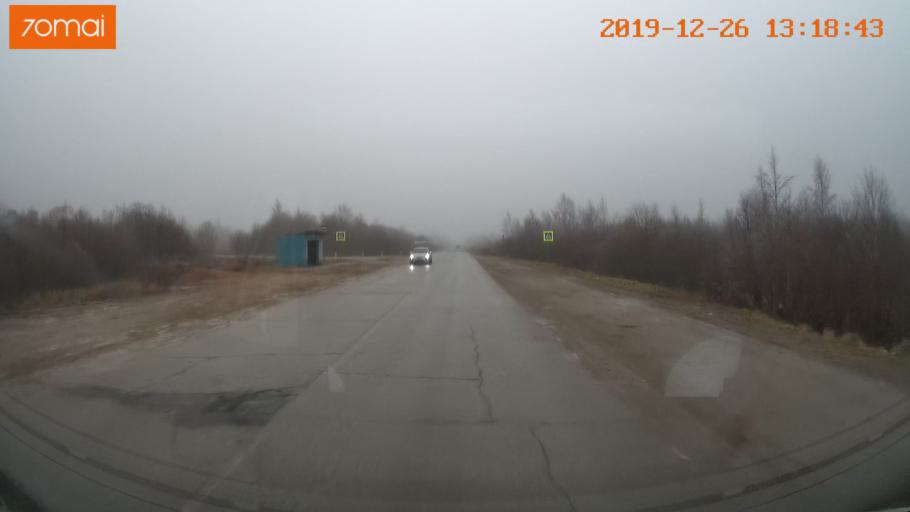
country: RU
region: Vologda
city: Cherepovets
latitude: 58.9513
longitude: 38.1246
